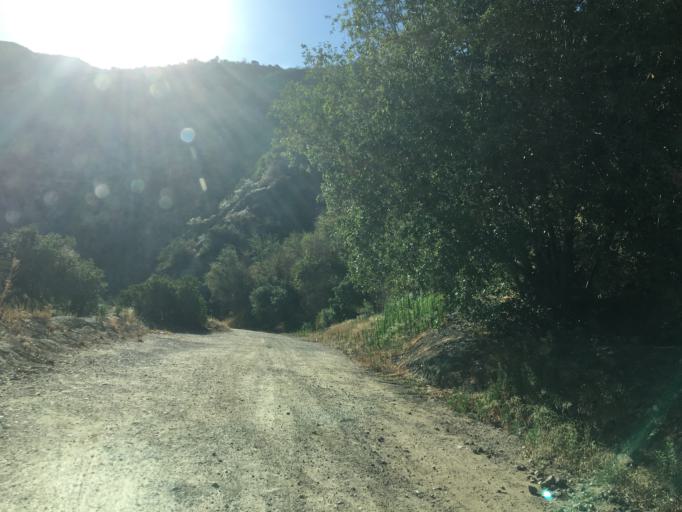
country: US
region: California
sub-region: Los Angeles County
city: Azusa
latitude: 34.1611
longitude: -117.8922
